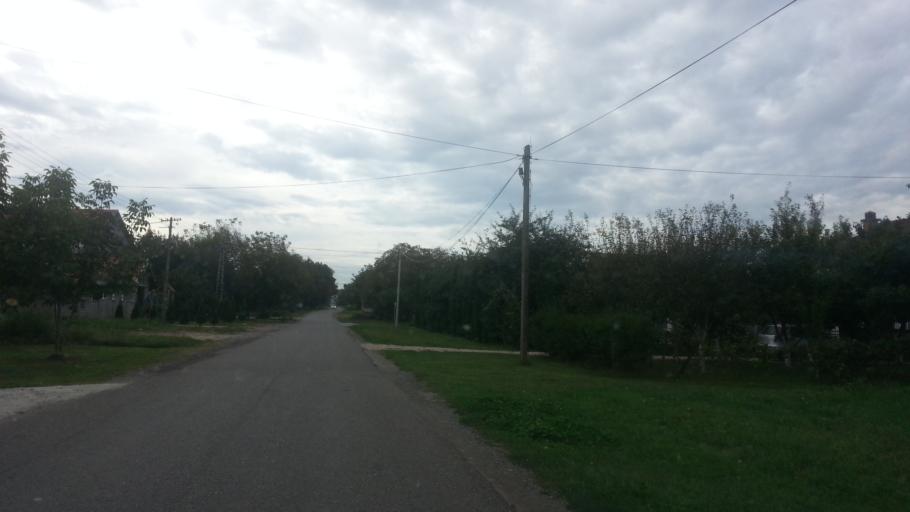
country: RS
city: Novi Banovci
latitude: 44.9637
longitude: 20.2752
